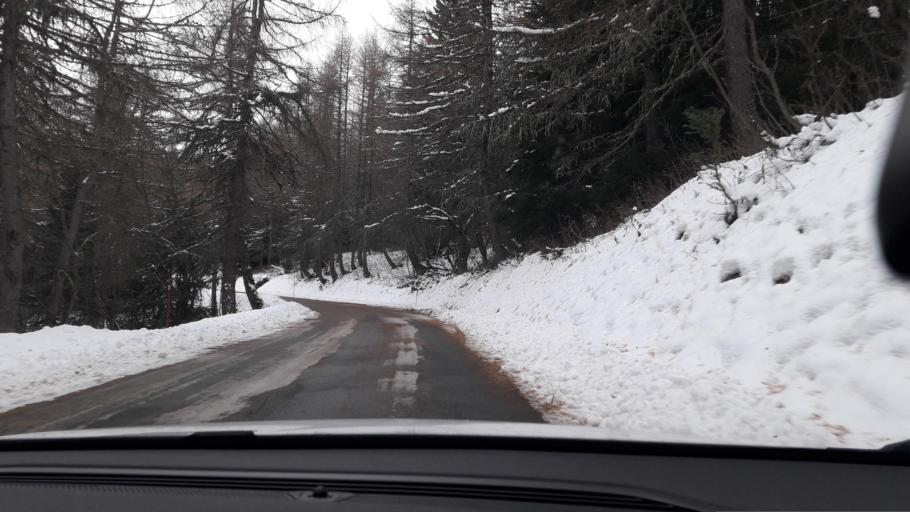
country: FR
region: Rhone-Alpes
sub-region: Departement de la Savoie
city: Saint-Michel-de-Maurienne
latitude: 45.2207
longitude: 6.4178
